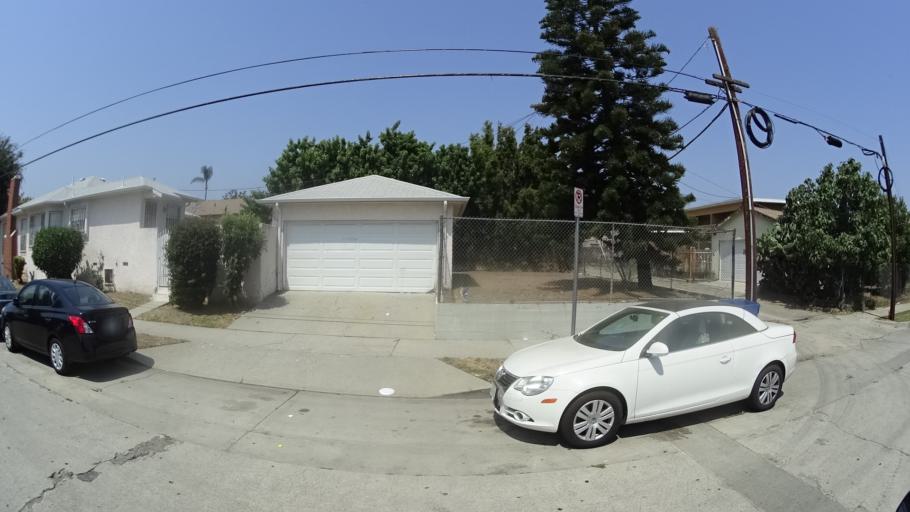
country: US
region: California
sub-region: Los Angeles County
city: Inglewood
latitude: 33.9731
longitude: -118.3287
